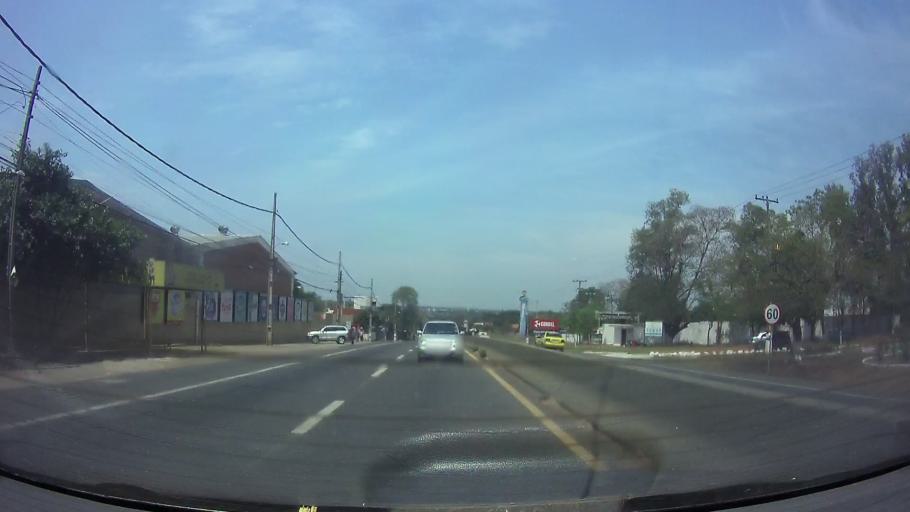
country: PY
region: Central
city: Itaugua
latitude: -25.3816
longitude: -57.3761
